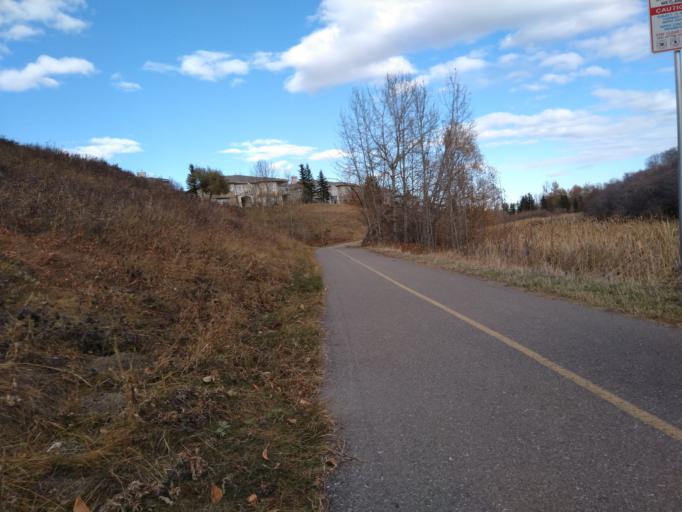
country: CA
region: Alberta
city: Calgary
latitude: 51.1377
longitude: -114.1344
